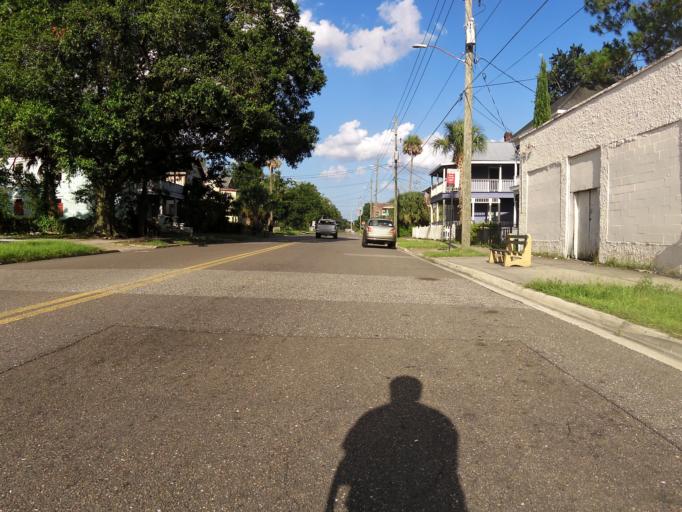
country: US
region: Florida
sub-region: Duval County
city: Jacksonville
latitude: 30.3361
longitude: -81.6502
